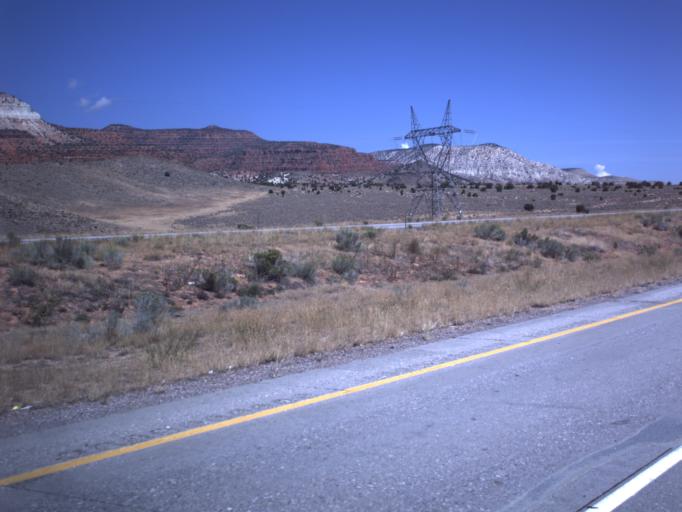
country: US
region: Utah
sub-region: Sevier County
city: Richfield
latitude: 38.8355
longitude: -112.0296
